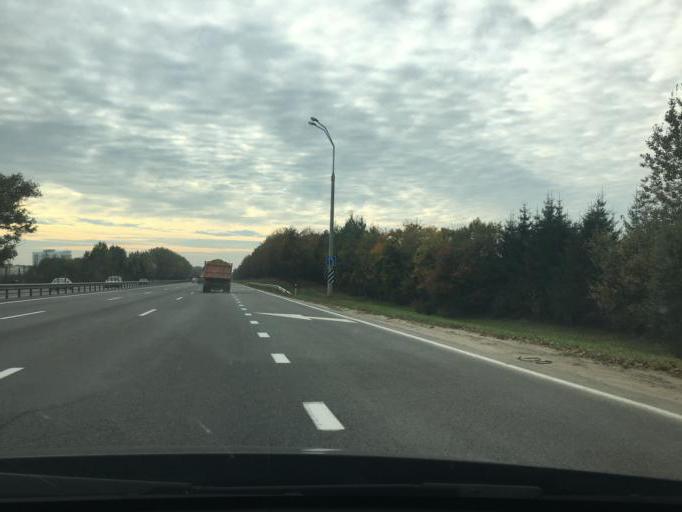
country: BY
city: Fanipol
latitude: 53.7518
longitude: 27.3253
